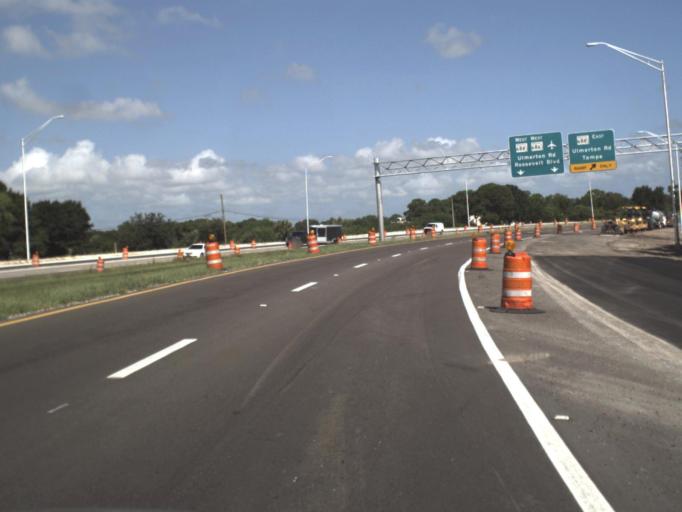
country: US
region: Florida
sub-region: Pinellas County
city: Feather Sound
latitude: 27.8888
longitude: -82.6721
